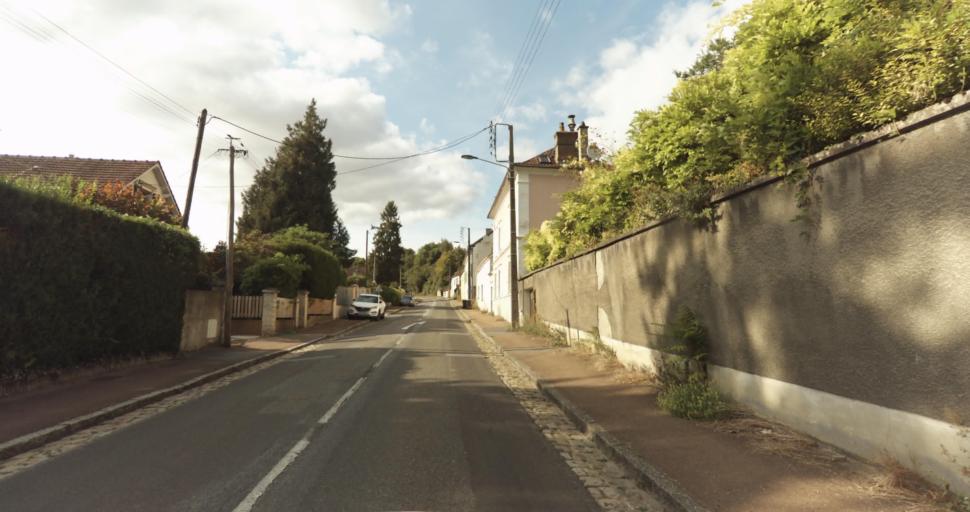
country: FR
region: Haute-Normandie
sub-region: Departement de l'Eure
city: Ivry-la-Bataille
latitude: 48.8848
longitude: 1.4552
